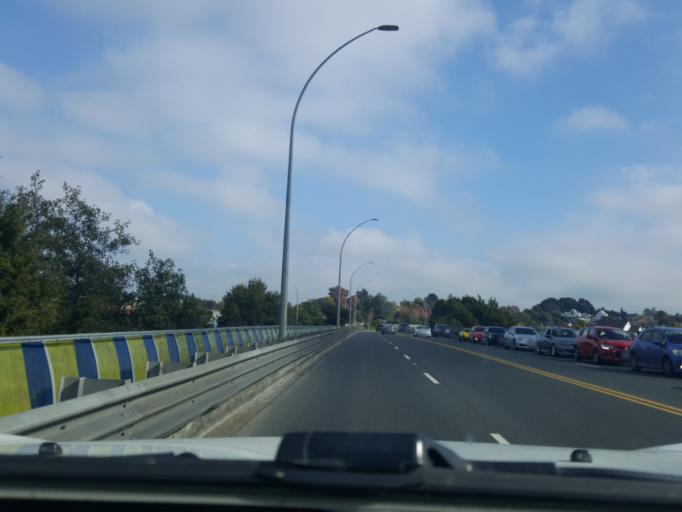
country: NZ
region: Waikato
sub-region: Hamilton City
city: Hamilton
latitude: -37.7424
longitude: 175.2552
